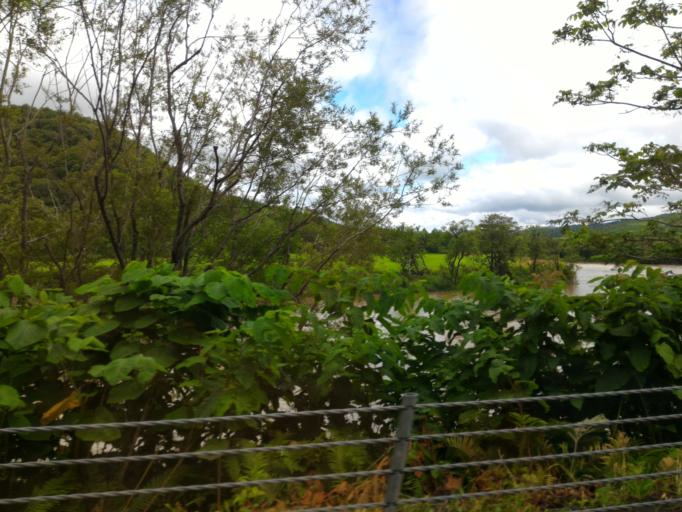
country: JP
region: Hokkaido
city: Nayoro
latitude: 44.7218
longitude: 142.2449
